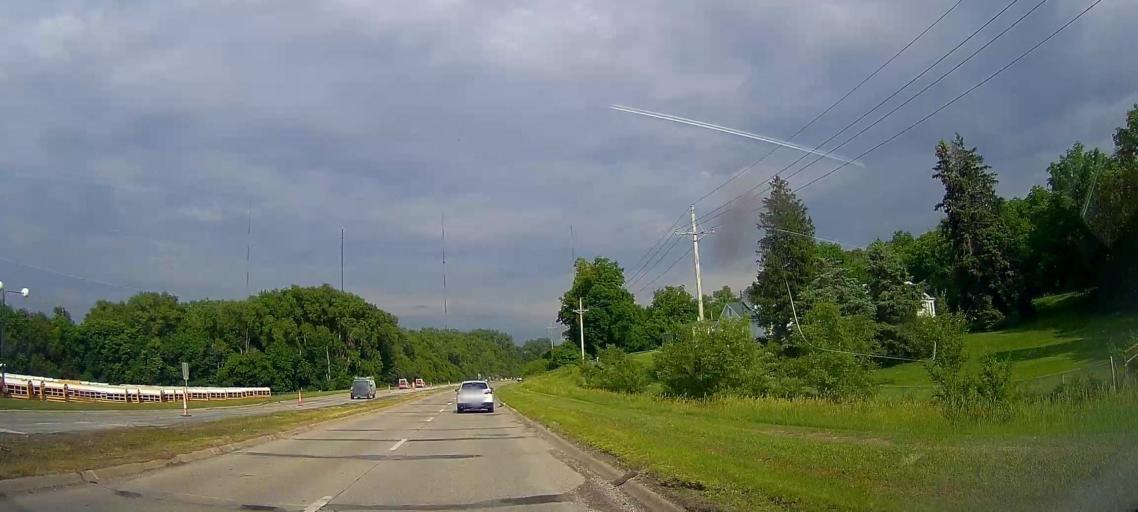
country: US
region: Nebraska
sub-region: Douglas County
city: Ralston
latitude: 41.3098
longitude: -96.0441
